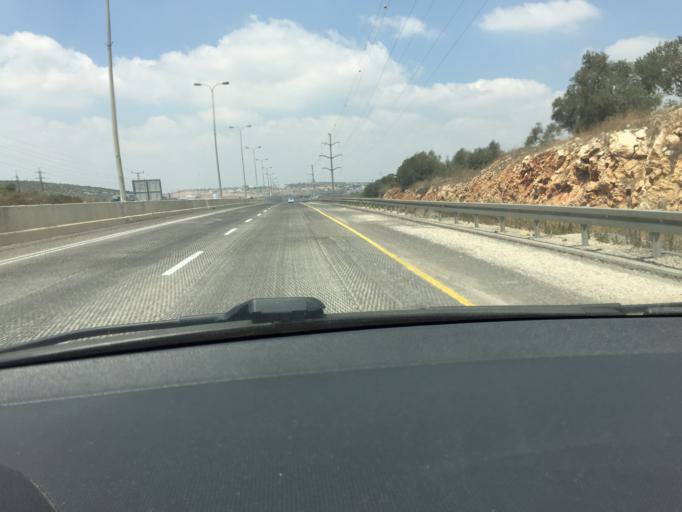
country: PS
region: West Bank
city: Kifil Haris
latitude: 32.1097
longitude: 35.1617
